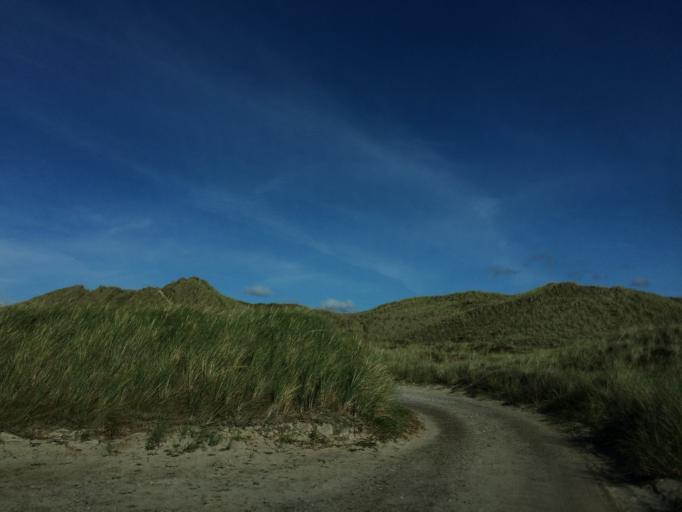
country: DK
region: Central Jutland
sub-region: Holstebro Kommune
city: Ulfborg
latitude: 56.2896
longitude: 8.1288
